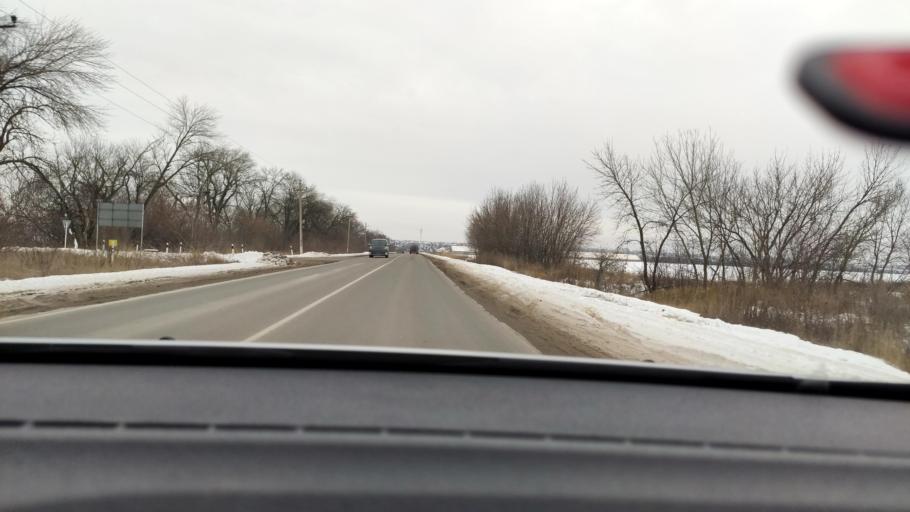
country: RU
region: Voronezj
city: Semiluki
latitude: 51.7277
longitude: 38.9867
